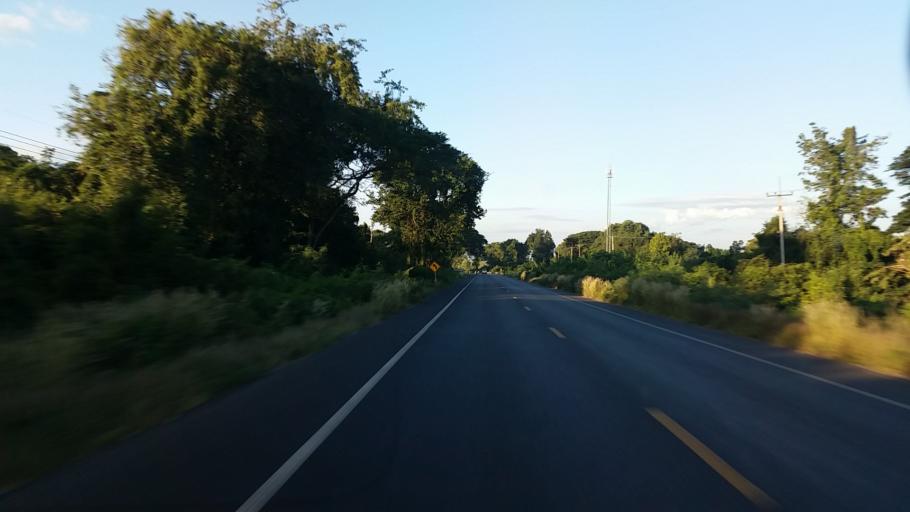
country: TH
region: Lop Buri
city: Chai Badan
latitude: 15.2588
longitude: 101.1835
